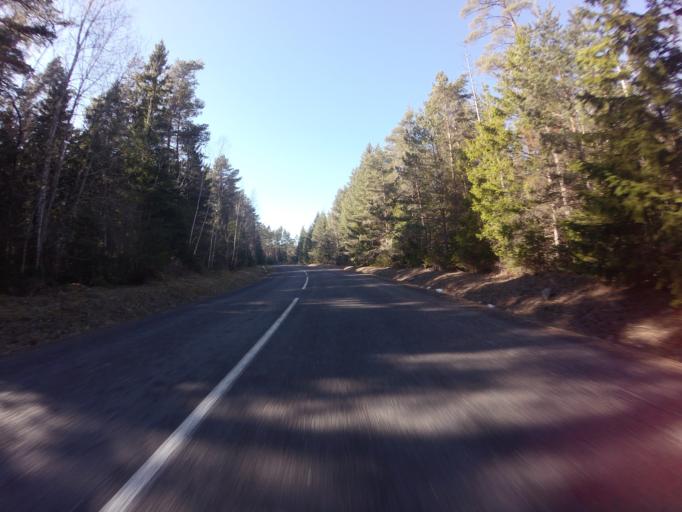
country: EE
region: Saare
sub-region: Kuressaare linn
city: Kuressaare
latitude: 58.5955
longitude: 22.5973
